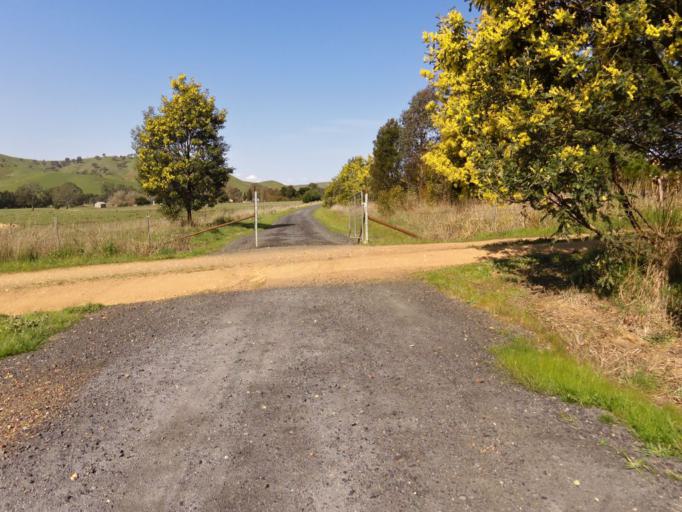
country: AU
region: Victoria
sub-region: Murrindindi
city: Alexandra
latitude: -37.0156
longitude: 145.7927
